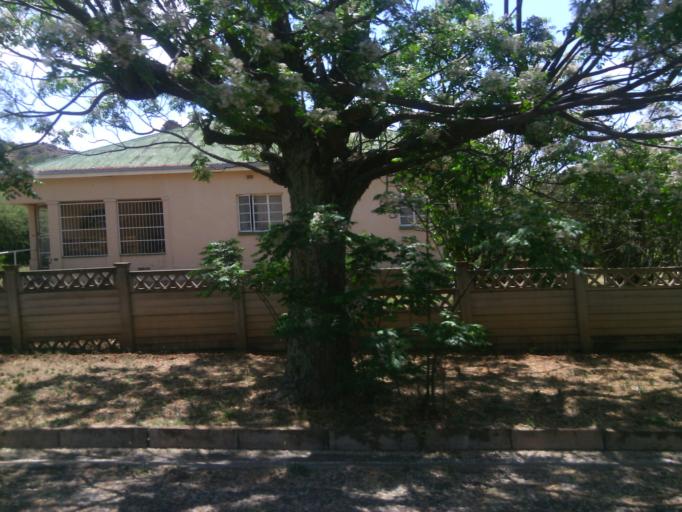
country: ZA
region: Orange Free State
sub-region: Xhariep District Municipality
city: Dewetsdorp
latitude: -29.5799
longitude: 26.6633
